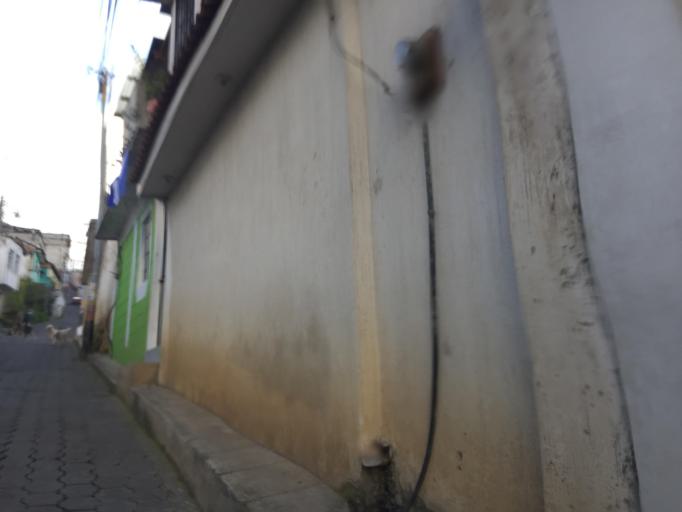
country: GT
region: Totonicapan
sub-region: Municipio de Totonicapan
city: Totonicapan
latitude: 14.9156
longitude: -91.3561
